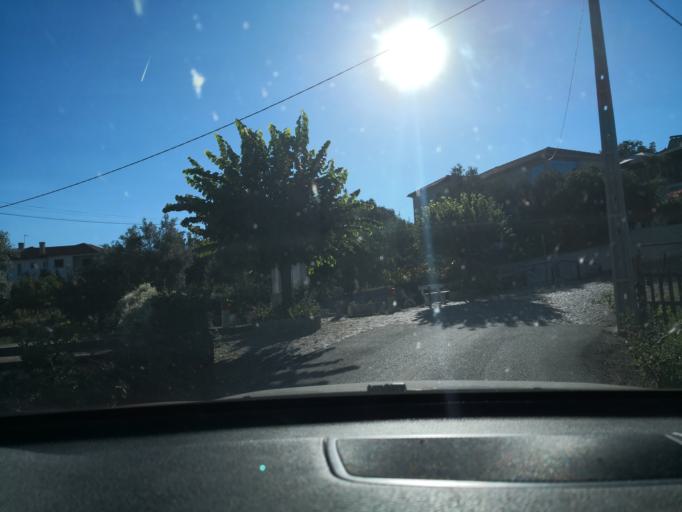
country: PT
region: Vila Real
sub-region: Sabrosa
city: Vilela
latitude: 41.2376
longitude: -7.6145
